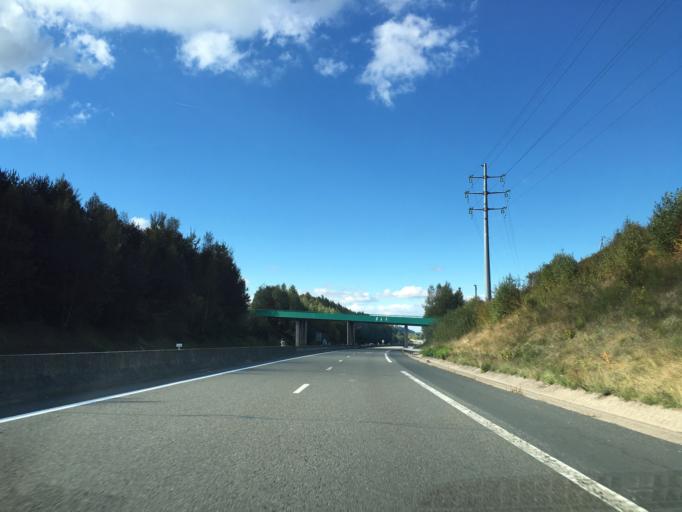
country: FR
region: Lorraine
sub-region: Departement des Vosges
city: Etival-Clairefontaine
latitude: 48.3989
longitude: 6.8282
